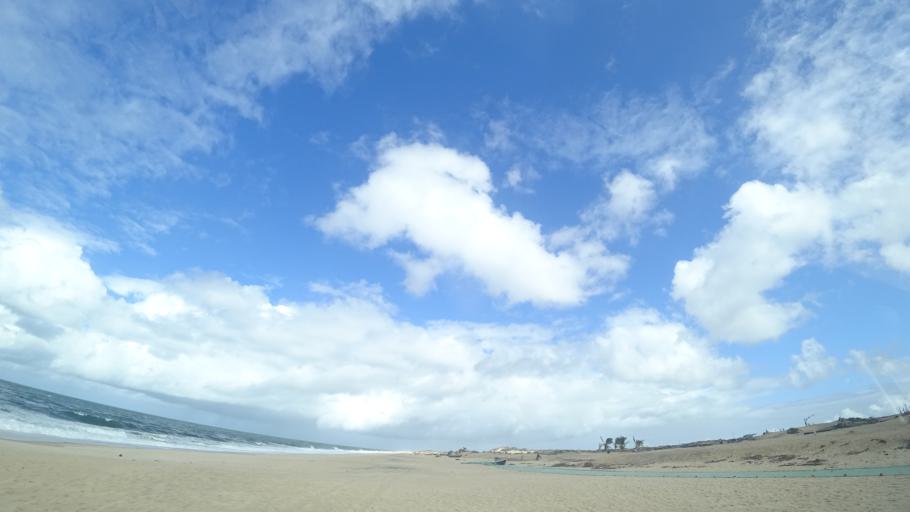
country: MZ
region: Sofala
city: Beira
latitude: -19.6489
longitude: 35.1808
